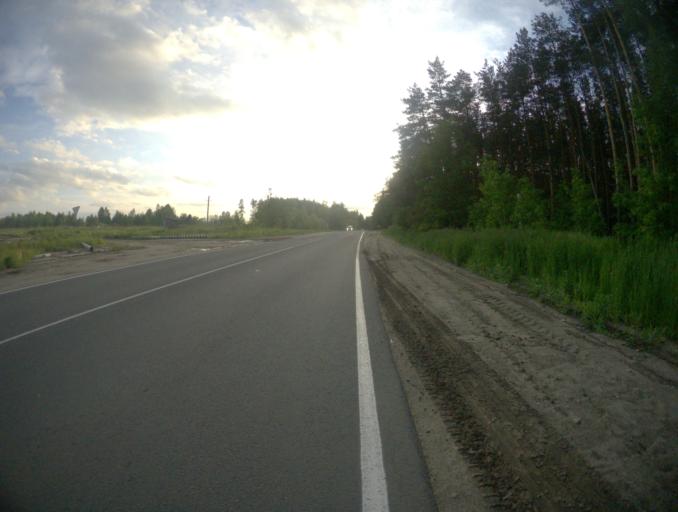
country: RU
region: Vladimir
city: Gus'-Khrustal'nyy
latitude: 55.6356
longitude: 40.7601
